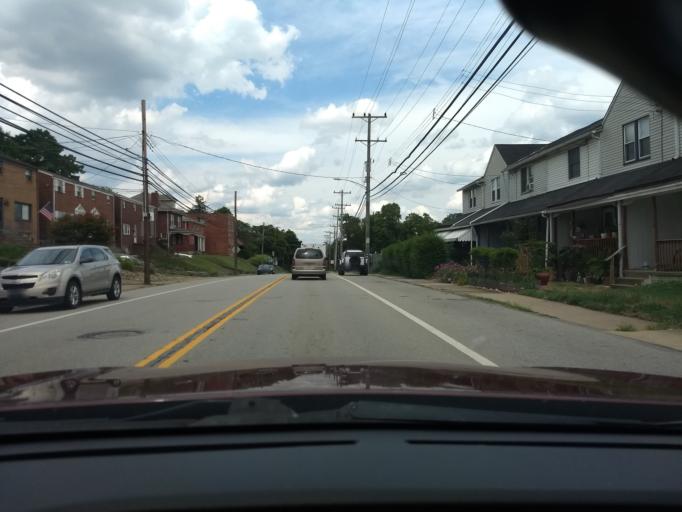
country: US
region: Pennsylvania
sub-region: Allegheny County
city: Blawnox
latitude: 40.4965
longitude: -79.8568
